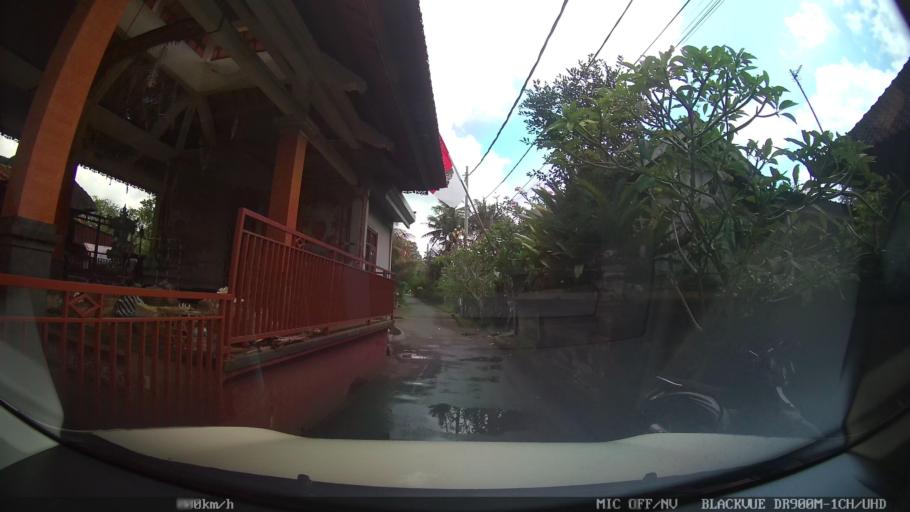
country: ID
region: Bali
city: Banjar Desa
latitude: -8.5777
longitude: 115.2656
